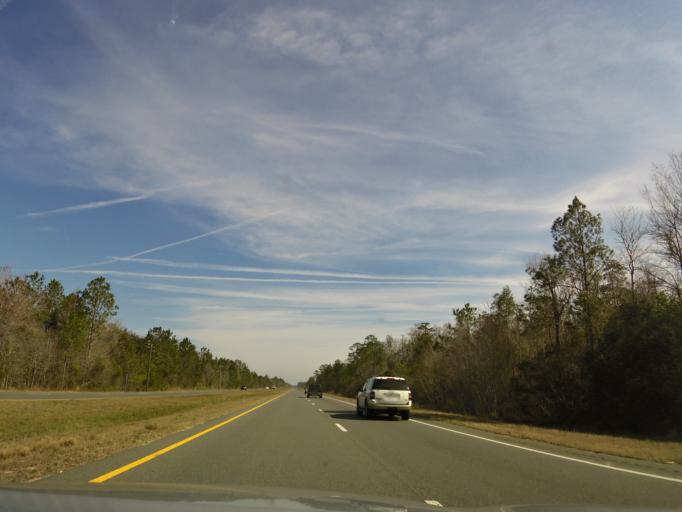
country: US
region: Georgia
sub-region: Brantley County
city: Nahunta
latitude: 31.1930
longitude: -82.0564
